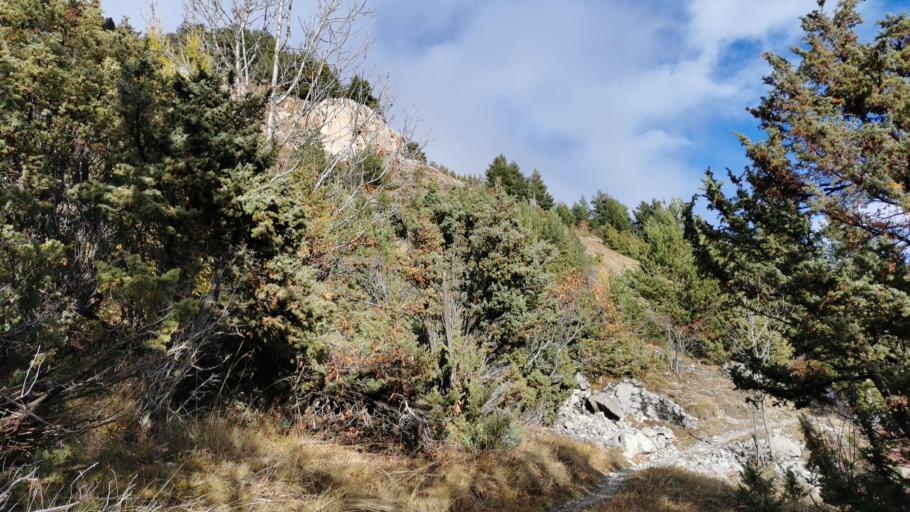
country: IT
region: Piedmont
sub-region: Provincia di Torino
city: Bardonecchia
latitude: 45.0238
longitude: 6.6192
